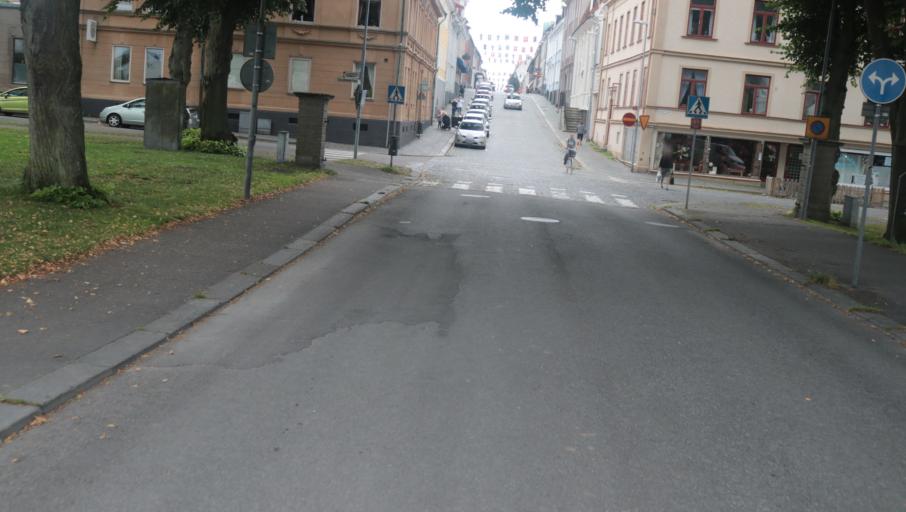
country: SE
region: Blekinge
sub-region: Karlshamns Kommun
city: Karlshamn
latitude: 56.1752
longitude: 14.8584
